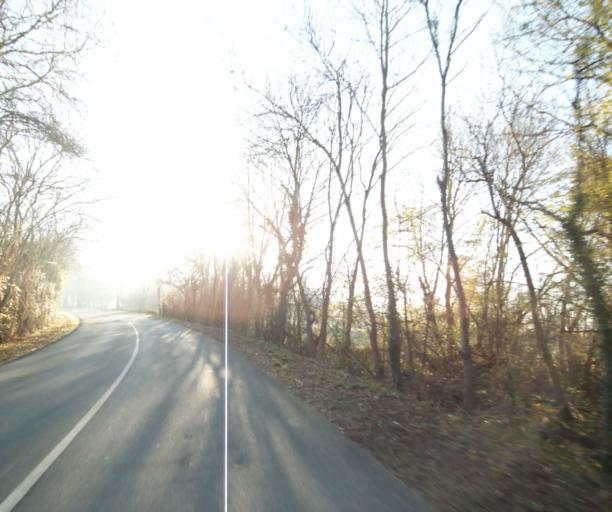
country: FR
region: Poitou-Charentes
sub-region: Departement de la Charente-Maritime
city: Cherac
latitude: 45.6890
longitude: -0.4660
